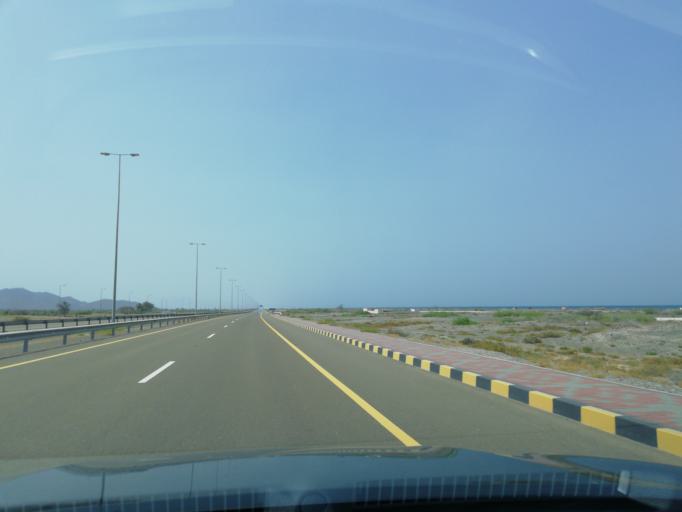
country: AE
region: Al Fujayrah
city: Al Fujayrah
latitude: 24.9284
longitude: 56.3846
